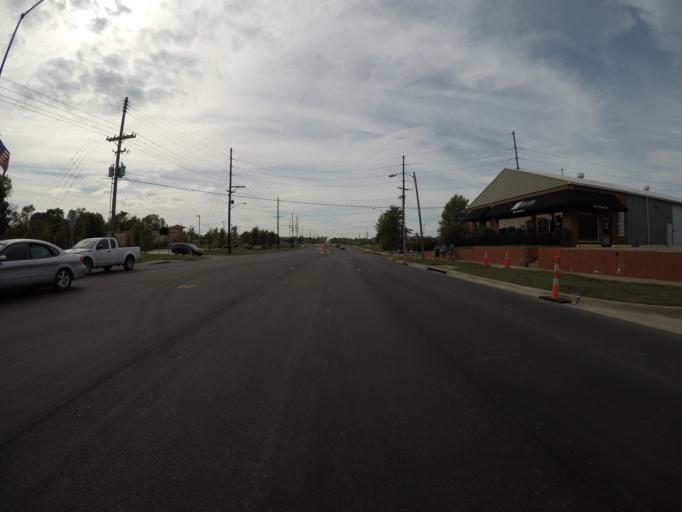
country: US
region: Kansas
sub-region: Johnson County
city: Olathe
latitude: 38.8838
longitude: -94.8317
